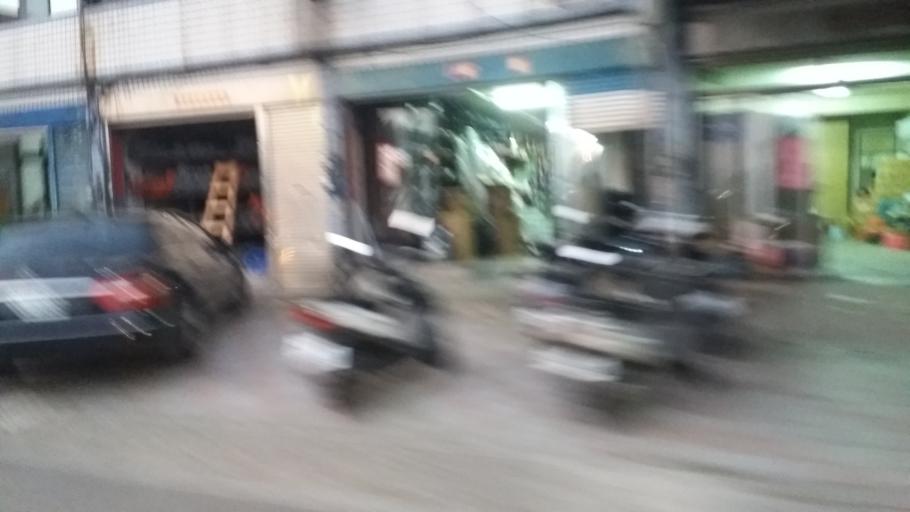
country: TW
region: Taiwan
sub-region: Hsinchu
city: Hsinchu
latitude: 24.7336
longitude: 120.9140
